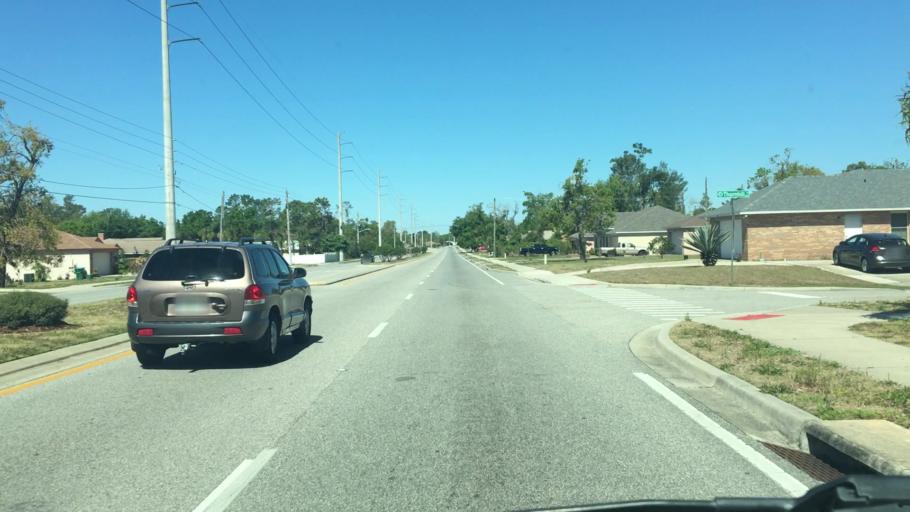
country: US
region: Florida
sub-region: Volusia County
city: Deltona
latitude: 28.9039
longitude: -81.1732
